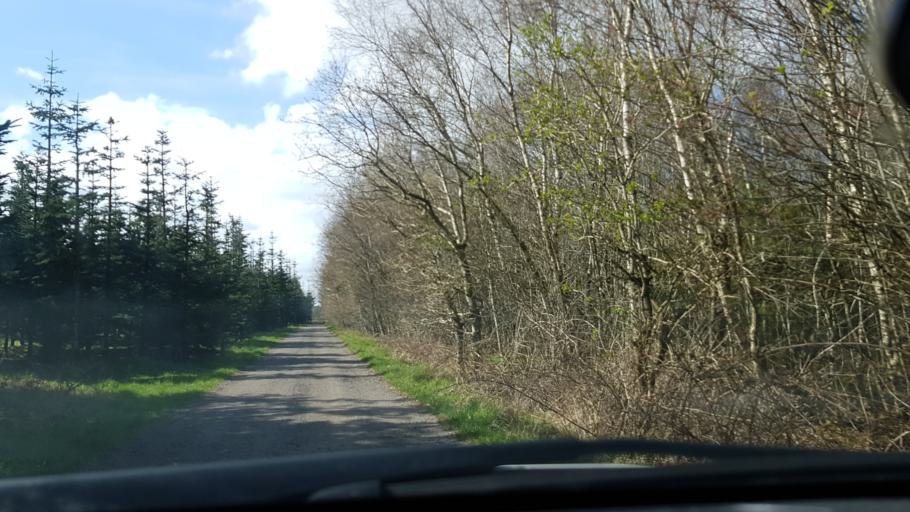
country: DK
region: South Denmark
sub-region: Haderslev Kommune
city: Gram
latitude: 55.3006
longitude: 8.9747
